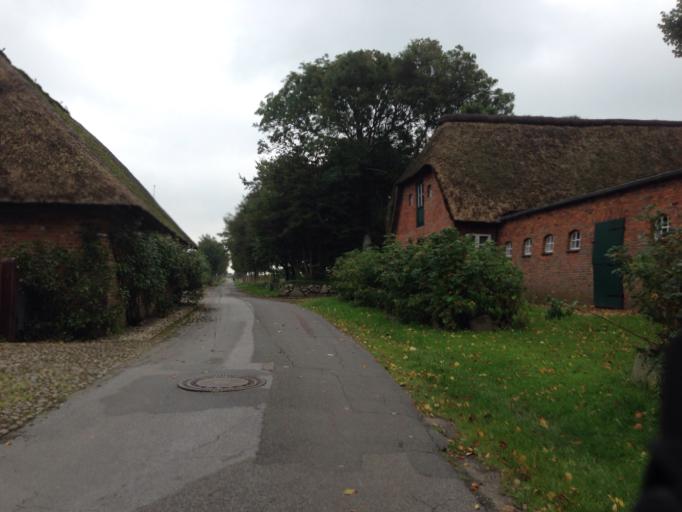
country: DE
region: Schleswig-Holstein
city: Alkersum
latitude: 54.7052
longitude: 8.5033
